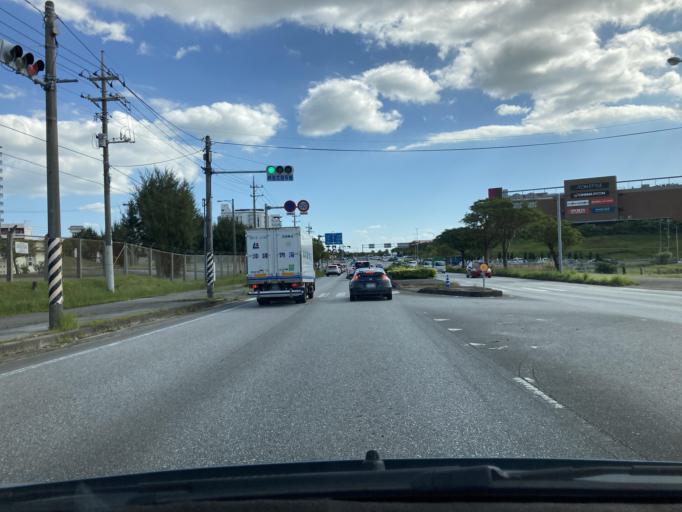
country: JP
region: Okinawa
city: Okinawa
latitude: 26.3168
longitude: 127.7919
